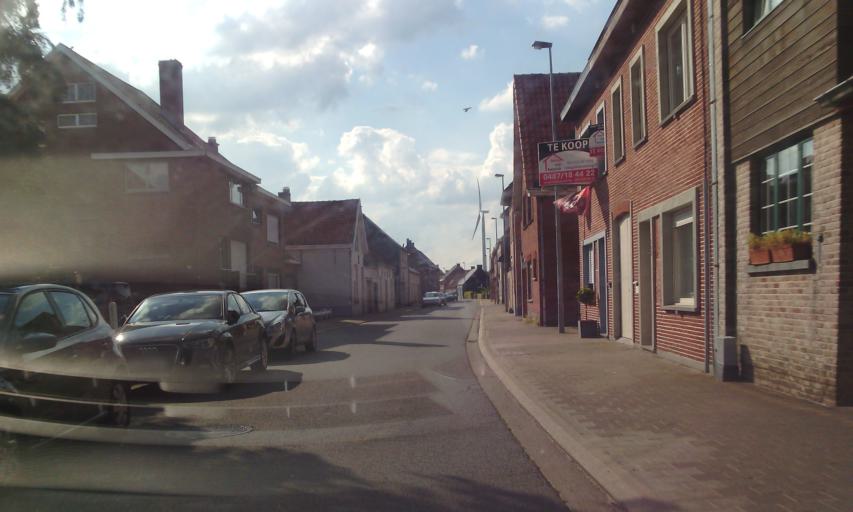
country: BE
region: Flanders
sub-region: Provincie Oost-Vlaanderen
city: Berlare
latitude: 51.0665
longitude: 3.9896
